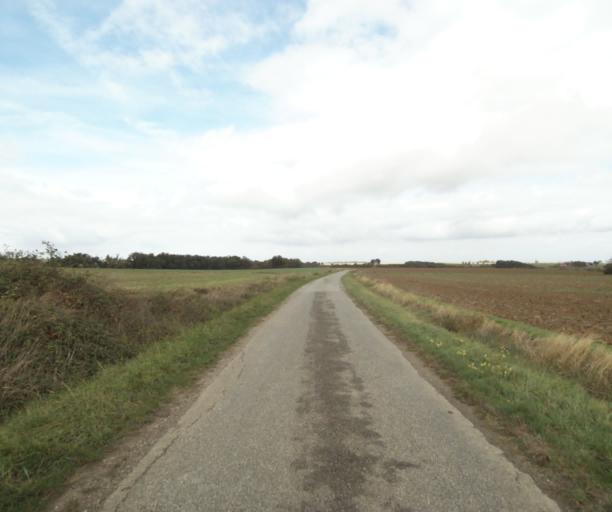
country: FR
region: Midi-Pyrenees
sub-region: Departement du Tarn-et-Garonne
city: Beaumont-de-Lomagne
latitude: 43.8715
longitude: 1.0888
